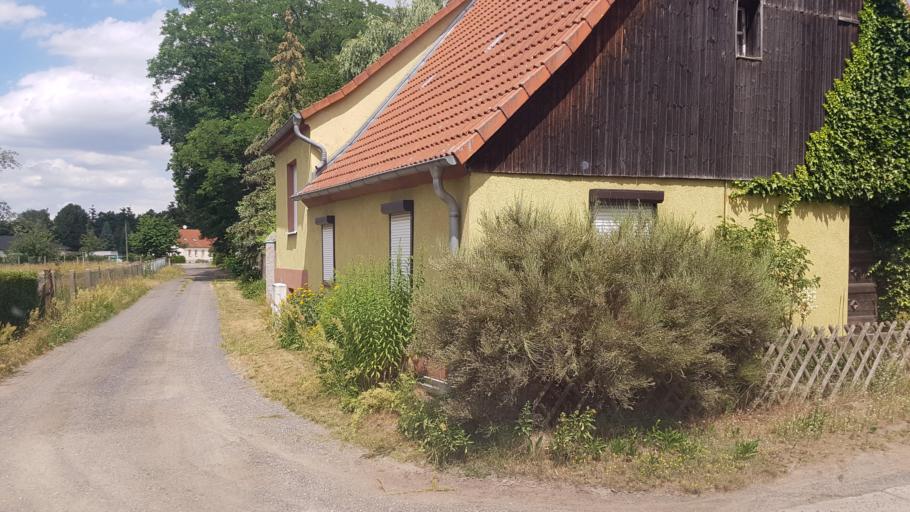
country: DE
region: Brandenburg
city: Luckenwalde
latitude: 52.0417
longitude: 13.1429
